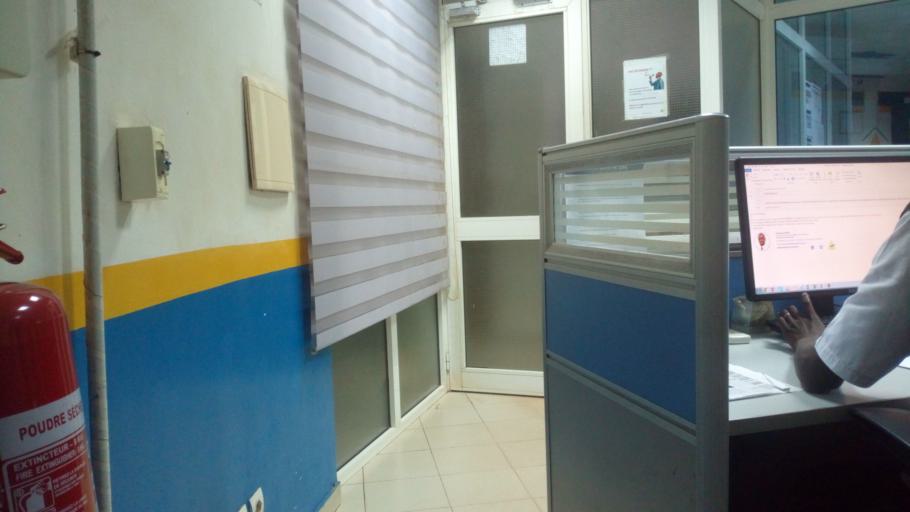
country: ML
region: Bamako
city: Bamako
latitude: 12.6400
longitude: -8.0320
